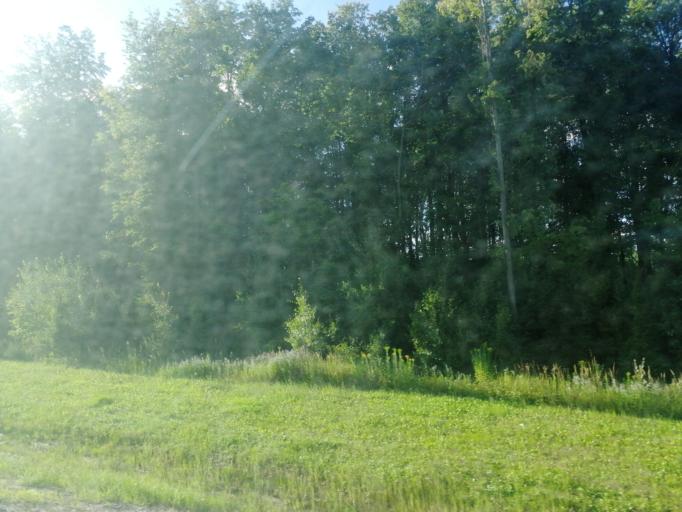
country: RU
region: Tula
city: Novogurovskiy
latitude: 54.2796
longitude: 37.2204
